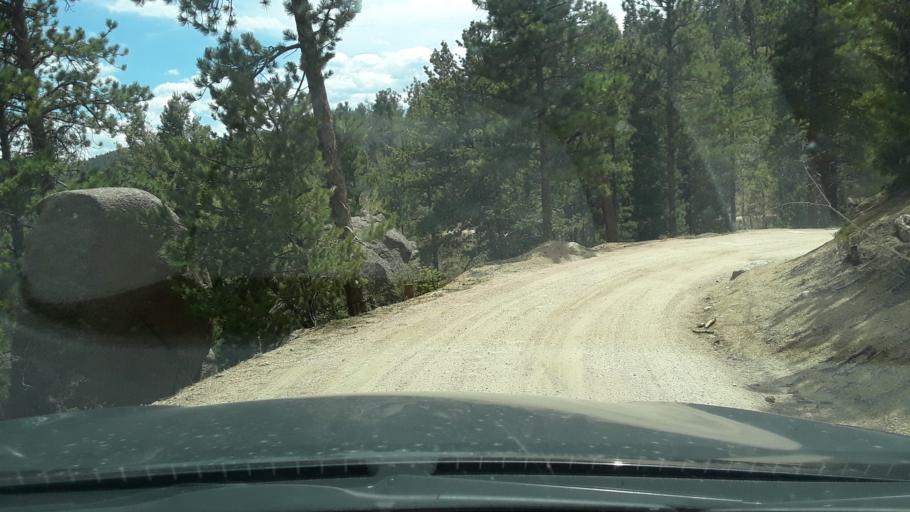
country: US
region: Colorado
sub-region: El Paso County
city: Palmer Lake
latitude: 39.0708
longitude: -104.9427
